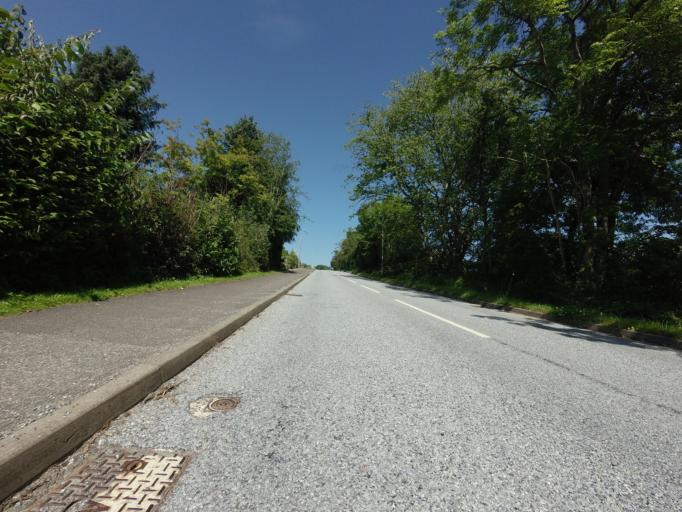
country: GB
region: Scotland
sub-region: Highland
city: Dingwall
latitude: 57.6081
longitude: -4.4214
